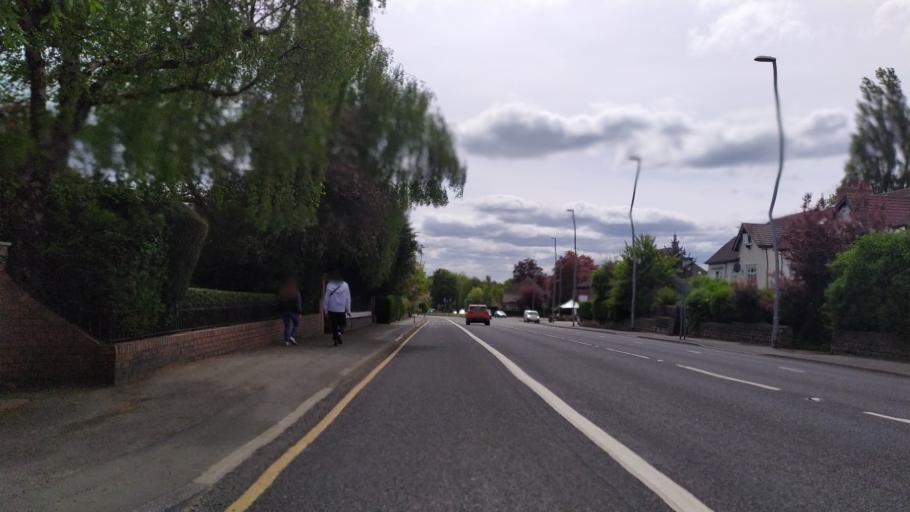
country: GB
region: England
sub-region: City and Borough of Leeds
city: Horsforth
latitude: 53.8348
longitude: -1.5932
